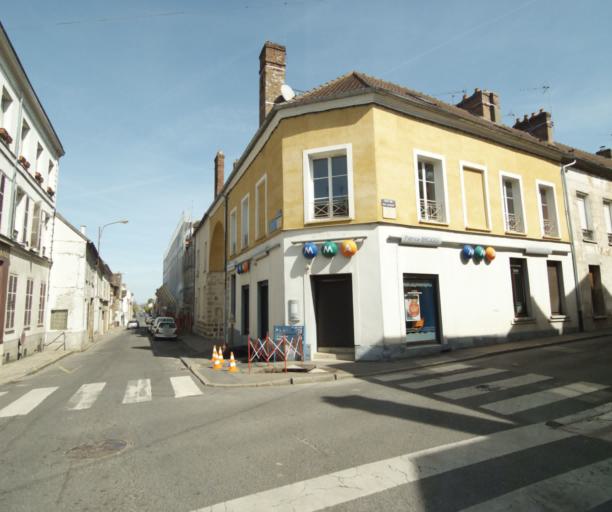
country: FR
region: Ile-de-France
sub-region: Departement de Seine-et-Marne
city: Nangis
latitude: 48.5563
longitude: 3.0137
